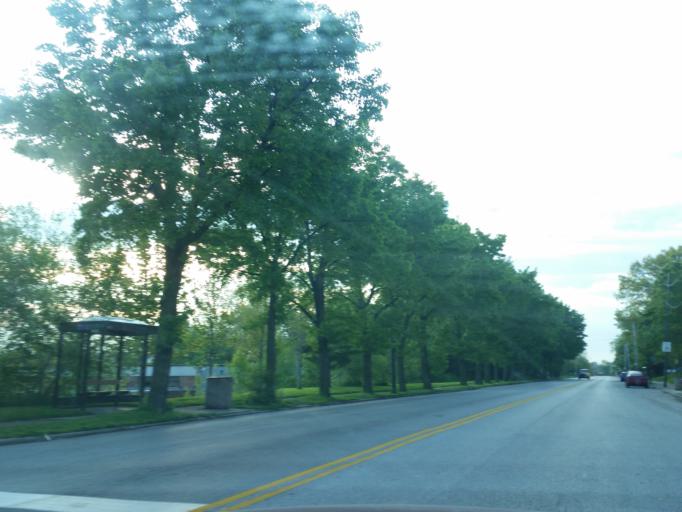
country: US
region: Ohio
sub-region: Cuyahoga County
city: Lakewood
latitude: 41.4821
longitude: -81.7627
